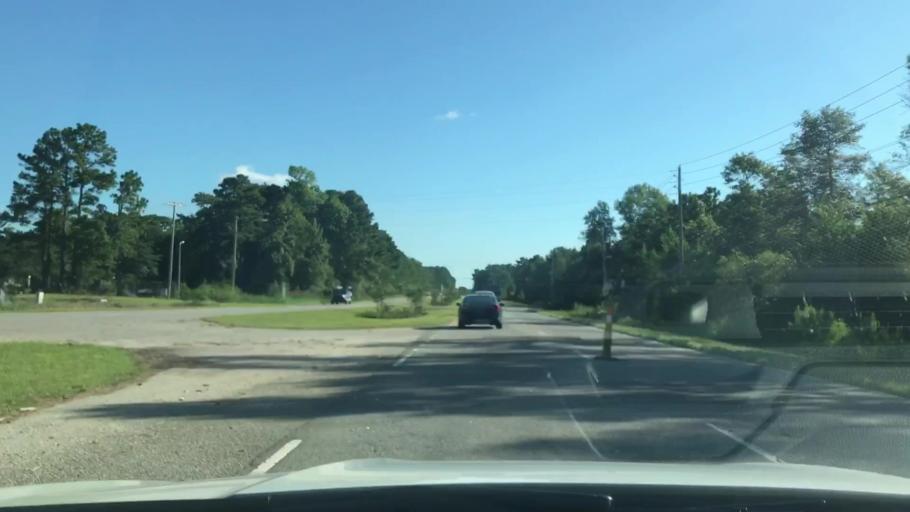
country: US
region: South Carolina
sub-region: Georgetown County
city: Georgetown
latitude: 33.3334
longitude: -79.3094
